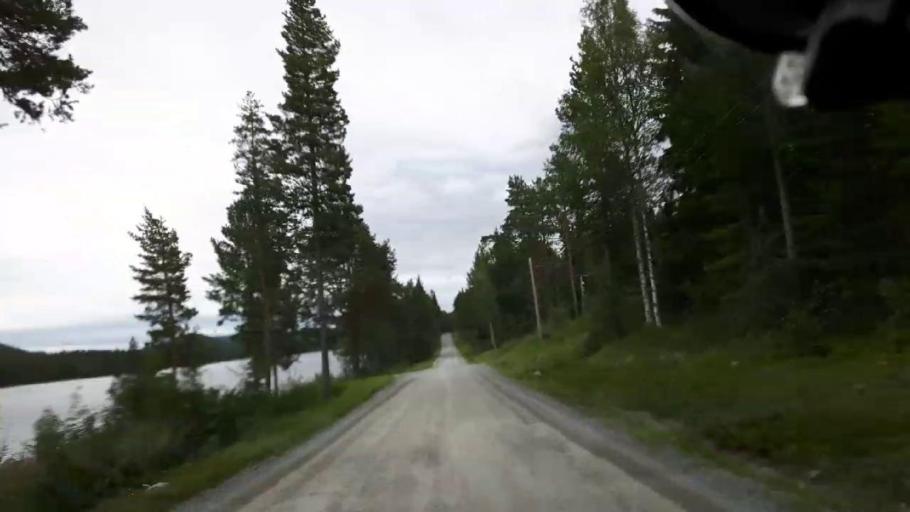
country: SE
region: Jaemtland
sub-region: Braecke Kommun
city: Braecke
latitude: 63.0918
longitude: 15.2532
